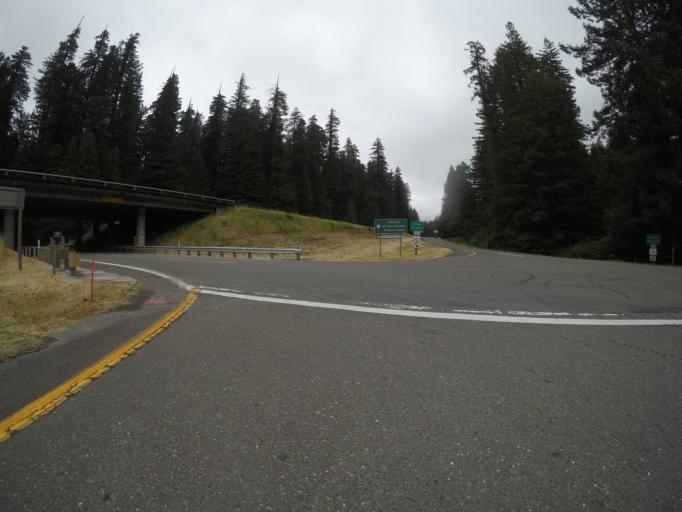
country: US
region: California
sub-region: Humboldt County
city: Rio Dell
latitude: 40.4396
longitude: -124.0322
